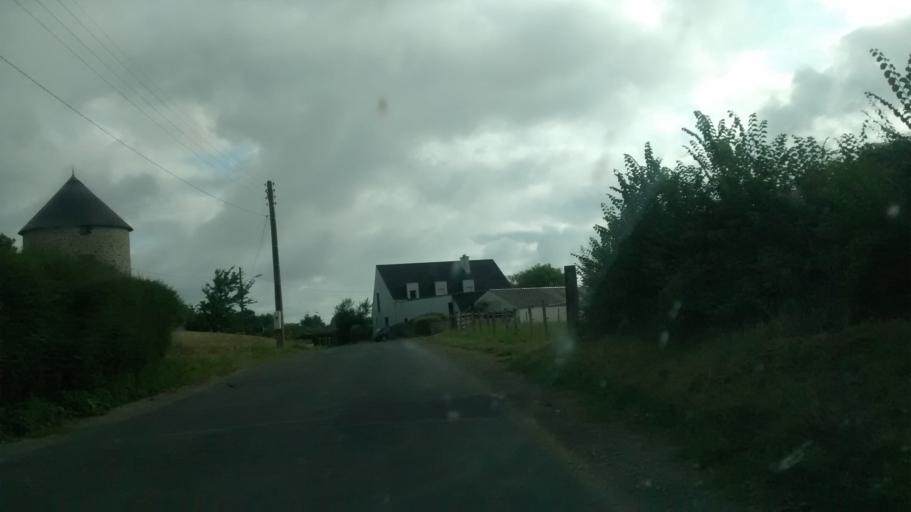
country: FR
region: Brittany
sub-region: Departement d'Ille-et-Vilaine
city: La Gouesniere
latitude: 48.5940
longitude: -1.8988
